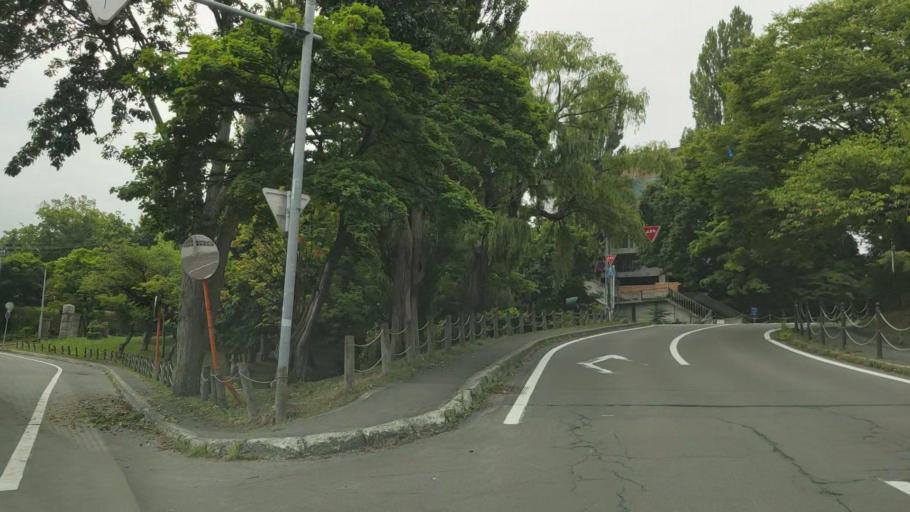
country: JP
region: Hokkaido
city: Otaru
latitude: 43.1903
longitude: 140.9937
